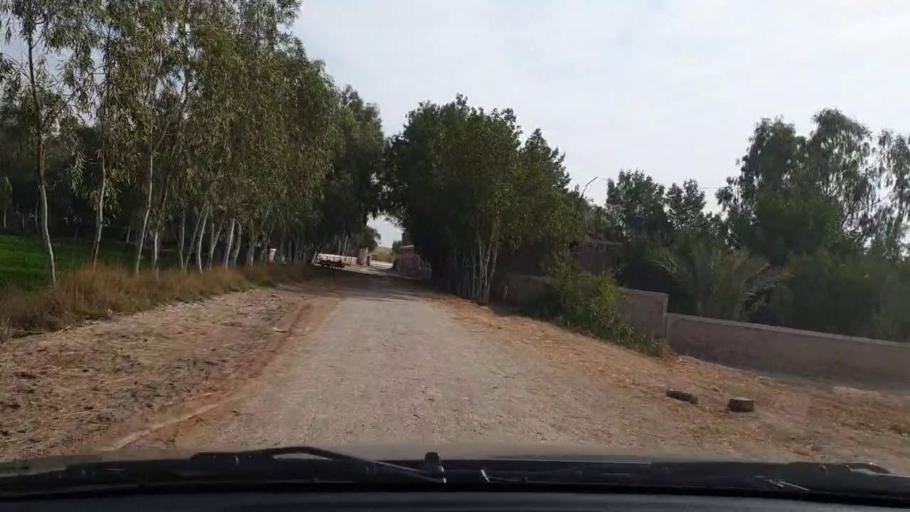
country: PK
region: Sindh
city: Shahpur Chakar
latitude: 26.1767
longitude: 68.6758
